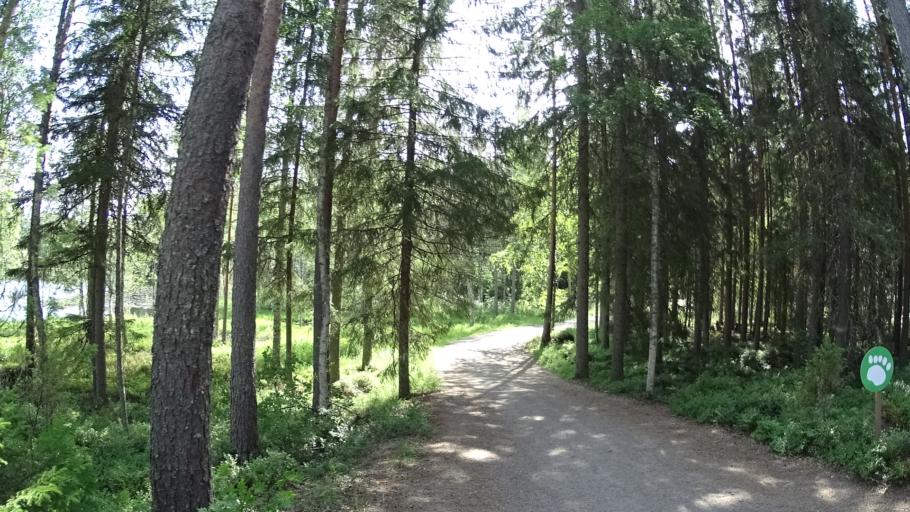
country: FI
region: Southern Ostrobothnia
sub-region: Kuusiokunnat
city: AEhtaeri
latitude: 62.5398
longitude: 24.1836
